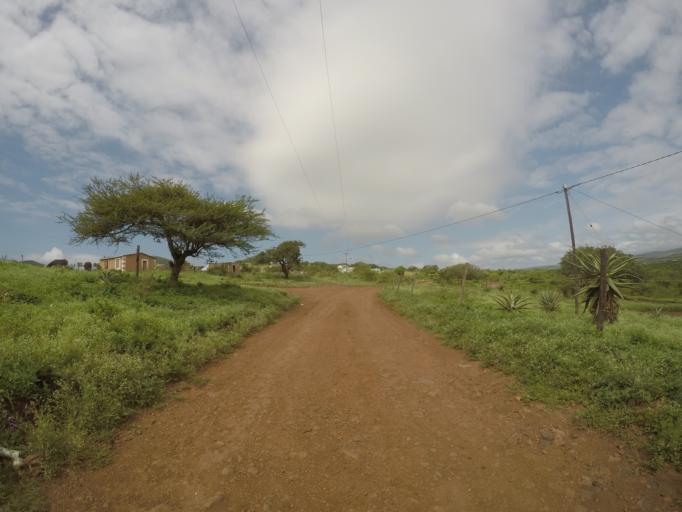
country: ZA
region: KwaZulu-Natal
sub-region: uThungulu District Municipality
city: Empangeni
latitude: -28.6209
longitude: 31.8718
